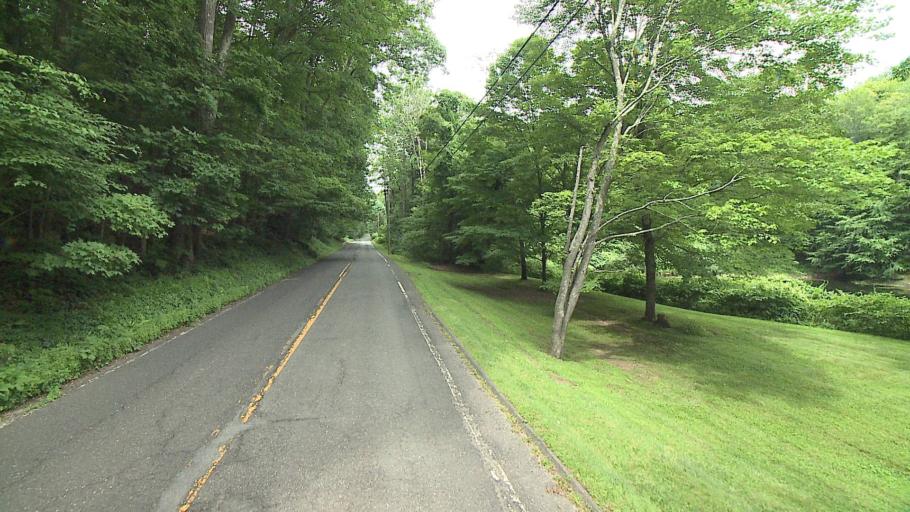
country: US
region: Connecticut
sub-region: Litchfield County
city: New Milford
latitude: 41.4963
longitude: -73.3549
